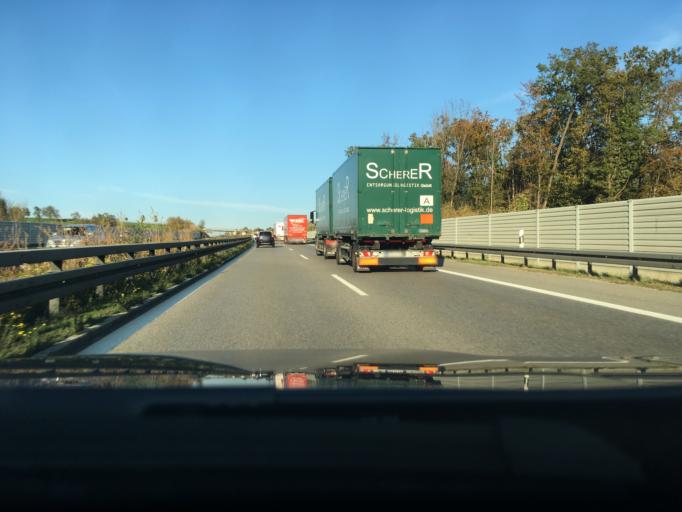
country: DE
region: Baden-Wuerttemberg
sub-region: Tuebingen Region
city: Kisslegg
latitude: 47.7384
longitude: 9.8904
